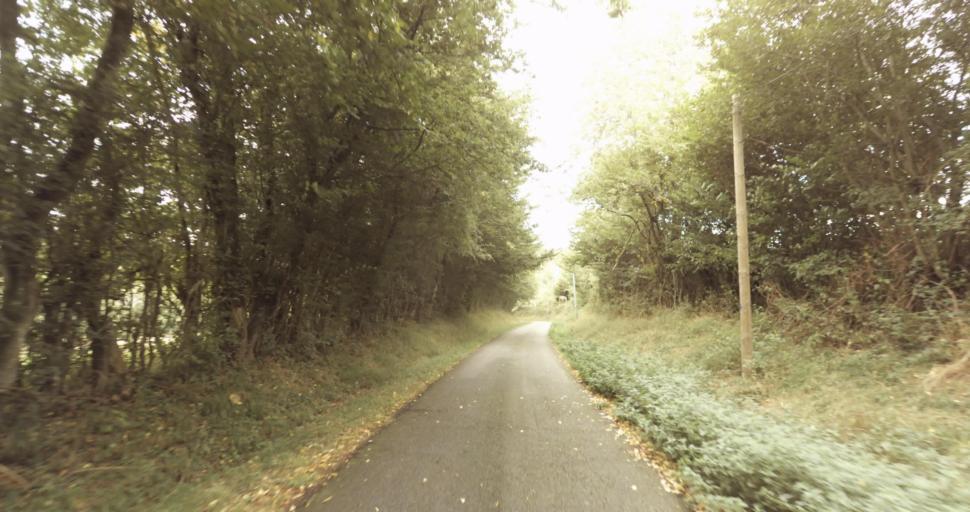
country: FR
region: Lower Normandy
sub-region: Departement de l'Orne
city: Gace
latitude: 48.7800
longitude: 0.3663
